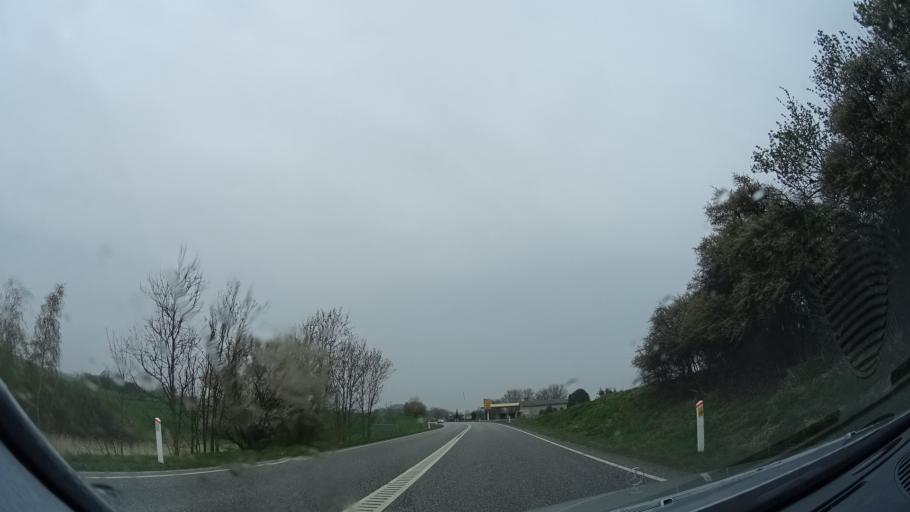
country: DK
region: Zealand
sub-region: Odsherred Kommune
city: Asnaes
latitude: 55.7935
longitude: 11.6009
